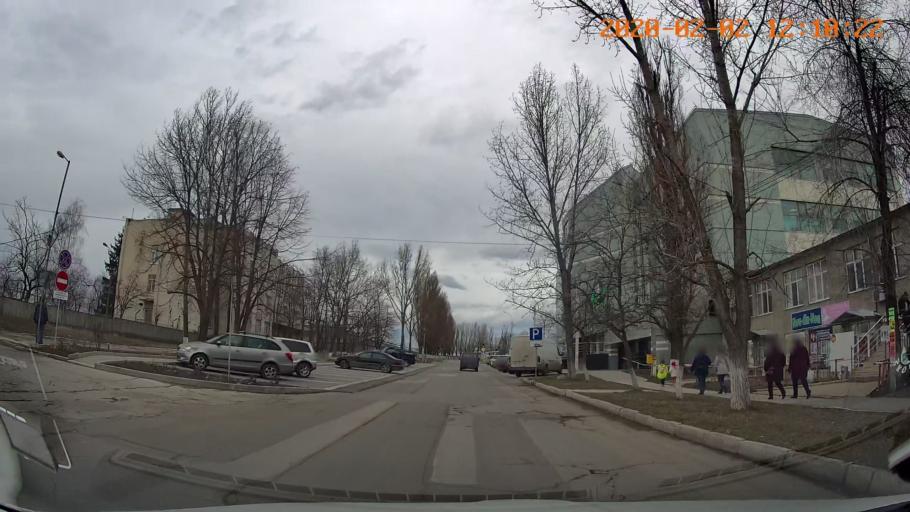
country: MD
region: Chisinau
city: Chisinau
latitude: 46.9997
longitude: 28.8043
